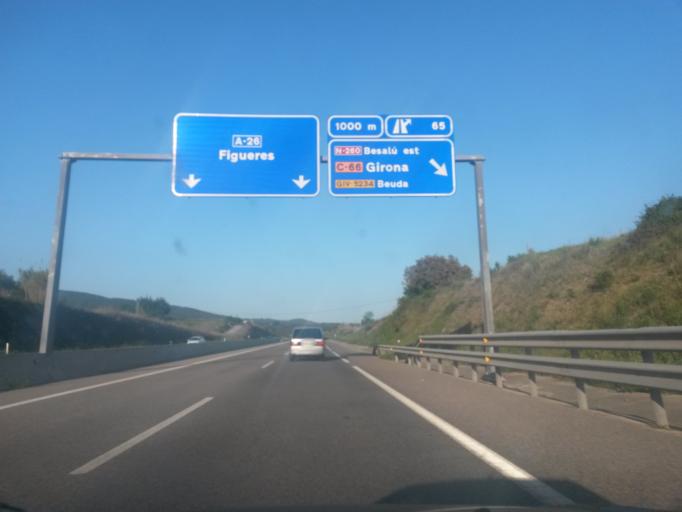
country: ES
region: Catalonia
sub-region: Provincia de Girona
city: Besalu
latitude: 42.2061
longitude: 2.6871
